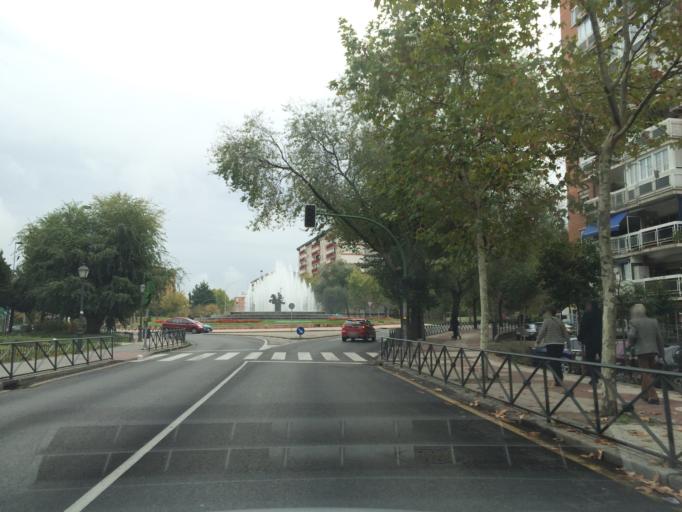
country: ES
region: Madrid
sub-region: Provincia de Madrid
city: Alcorcon
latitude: 40.3481
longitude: -3.8189
